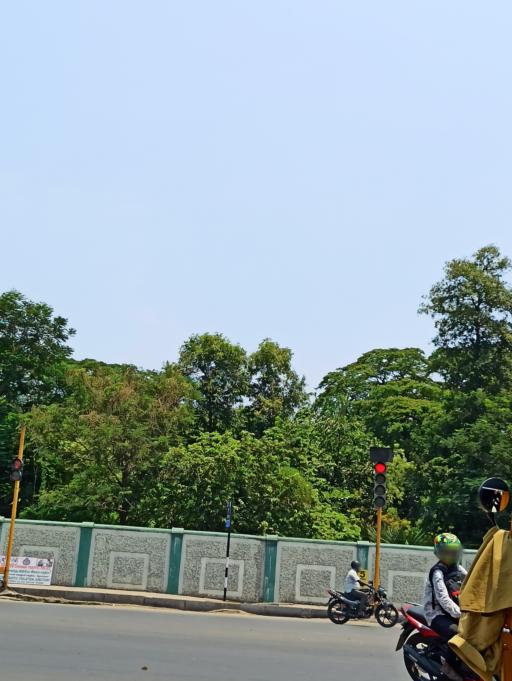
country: IN
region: Tamil Nadu
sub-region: Chennai
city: Chetput
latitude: 13.0759
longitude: 80.2340
